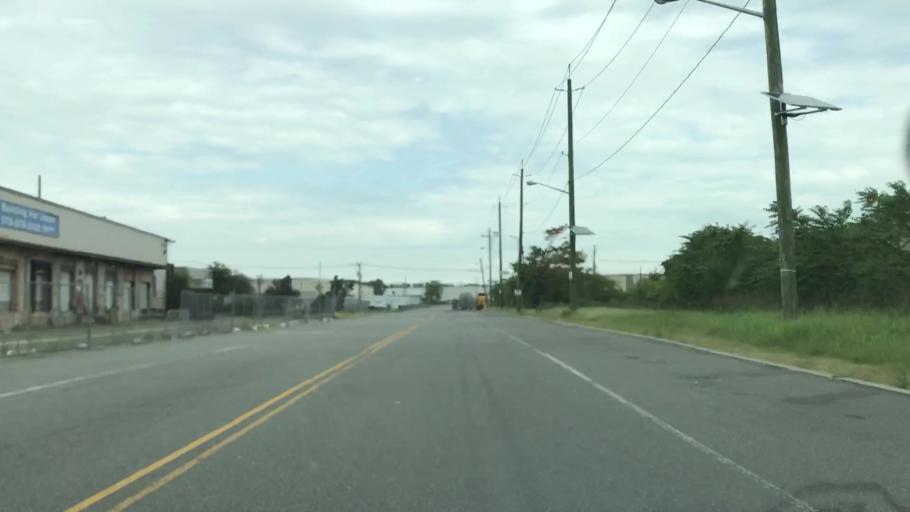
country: US
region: New Jersey
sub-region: Hudson County
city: Bayonne
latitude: 40.6760
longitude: -74.0953
